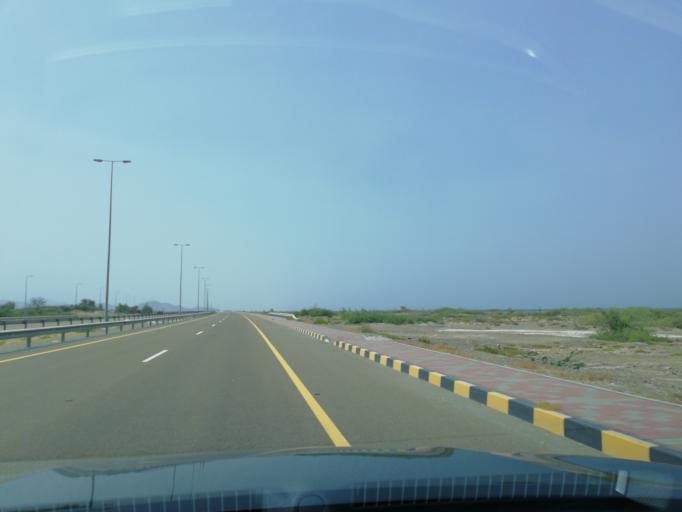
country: OM
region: Al Batinah
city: Shinas
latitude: 24.8908
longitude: 56.4011
